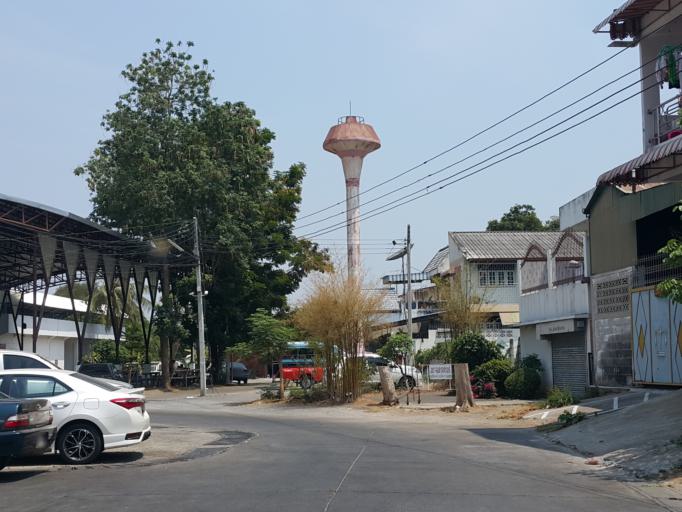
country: TH
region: Kanchanaburi
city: Kanchanaburi
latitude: 14.0228
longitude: 99.5279
